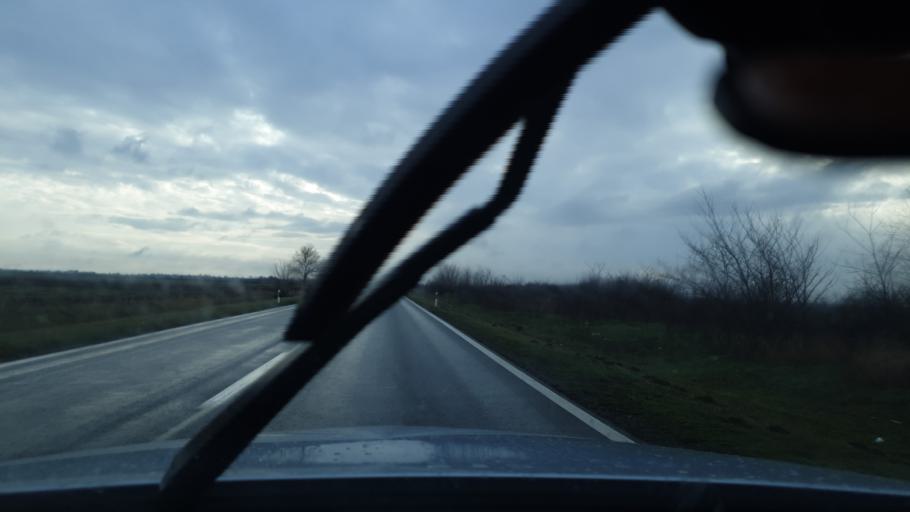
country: RS
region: Autonomna Pokrajina Vojvodina
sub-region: Juznobanatski Okrug
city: Kovin
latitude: 44.7798
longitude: 20.9319
